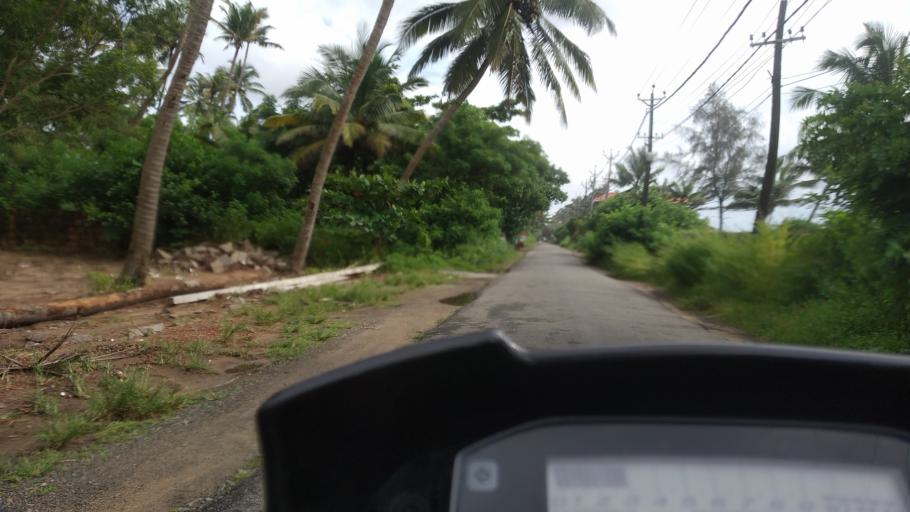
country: IN
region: Kerala
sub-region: Thrissur District
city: Kodungallur
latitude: 10.1466
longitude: 76.1769
